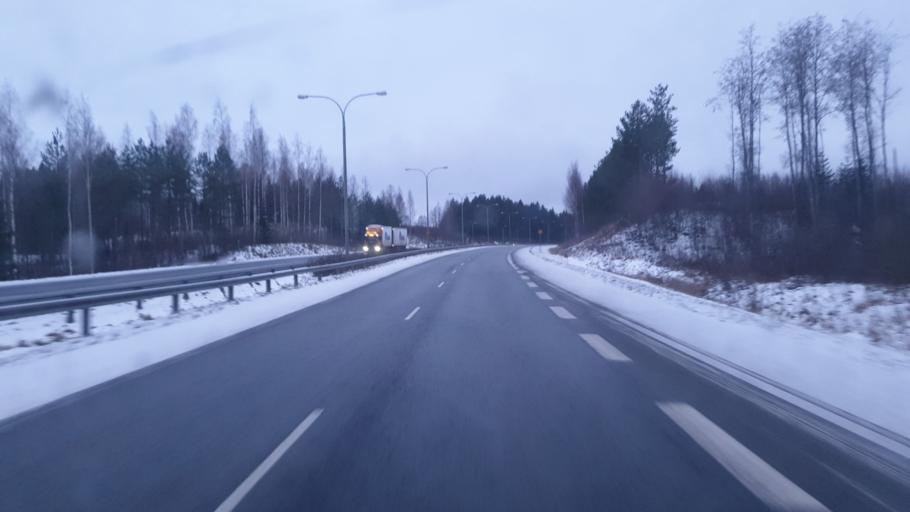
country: FI
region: Northern Savo
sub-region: Kuopio
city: Siilinjaervi
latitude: 63.0575
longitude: 27.6714
